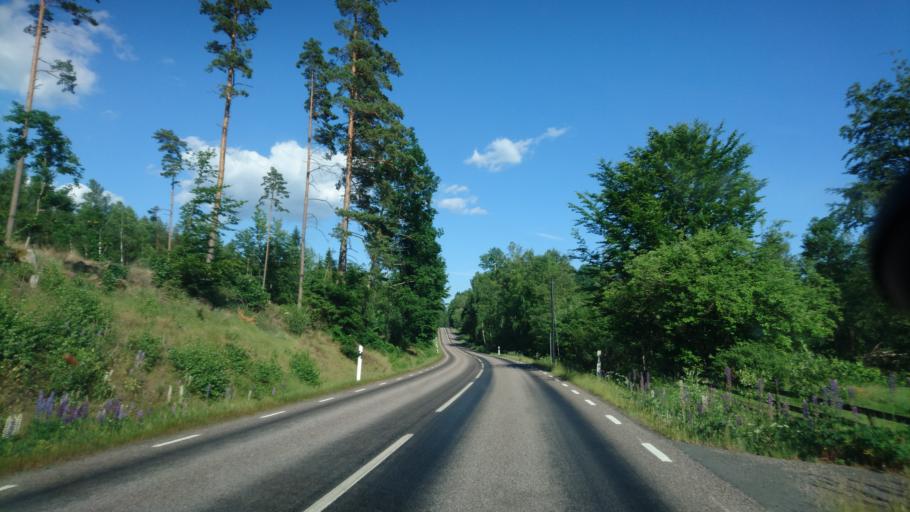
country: SE
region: Skane
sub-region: Osby Kommun
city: Lonsboda
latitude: 56.3914
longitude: 14.3405
